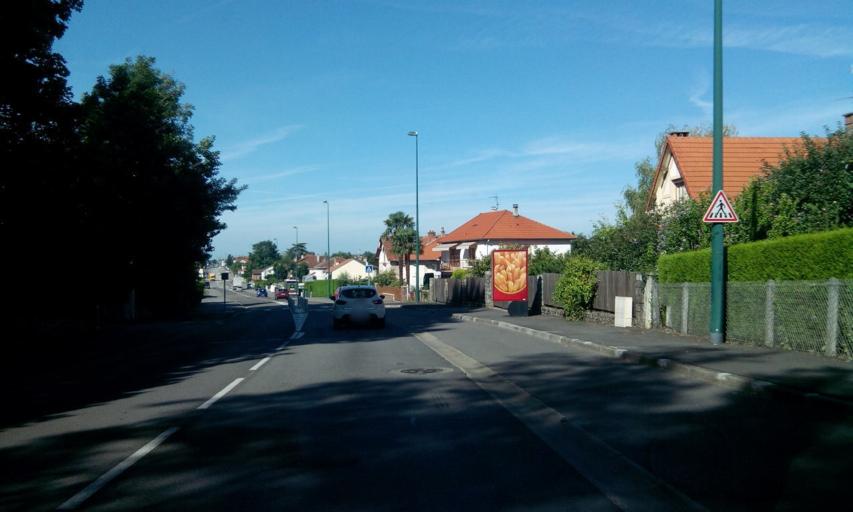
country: FR
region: Limousin
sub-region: Departement de la Haute-Vienne
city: Panazol
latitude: 45.8342
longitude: 1.3081
